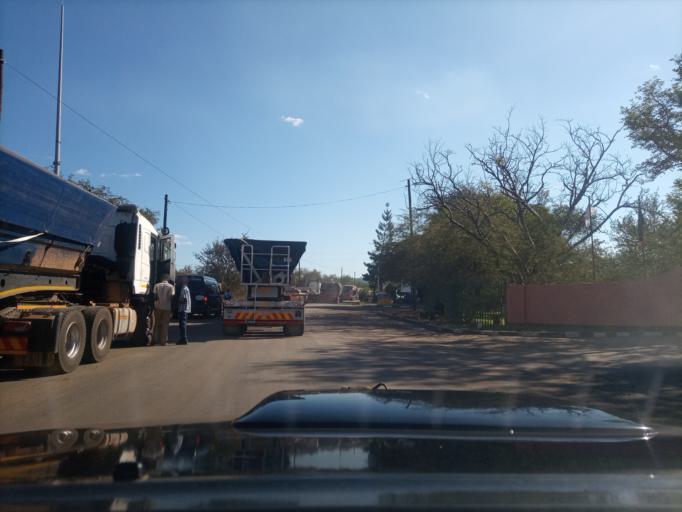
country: ZW
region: Matabeleland North
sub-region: Hwange District
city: Victoria Falls
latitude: -17.9285
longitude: 25.8642
